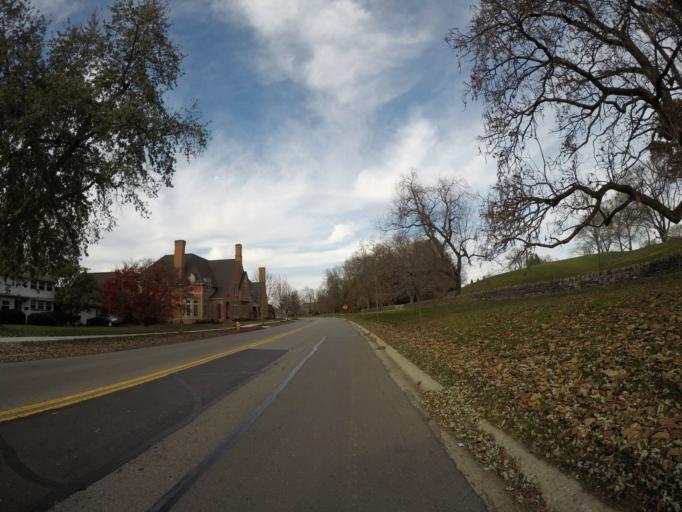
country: US
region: Ohio
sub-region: Franklin County
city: Upper Arlington
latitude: 39.9988
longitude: -83.0738
